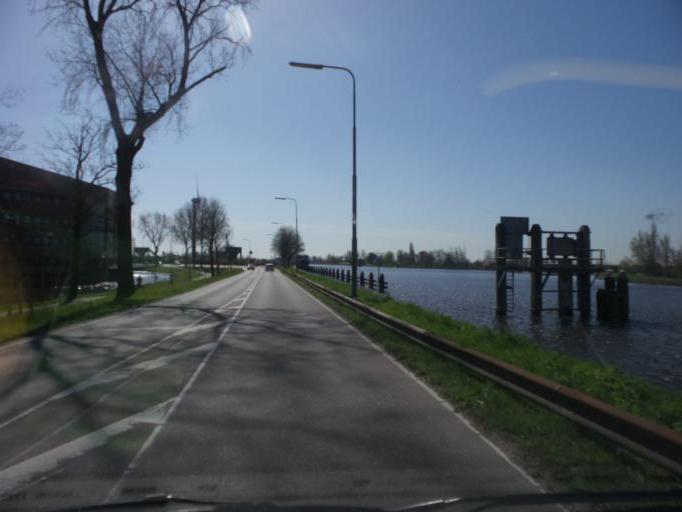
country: NL
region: South Holland
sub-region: Gemeente Gouda
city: Bloemendaal
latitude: 52.0172
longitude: 4.6834
